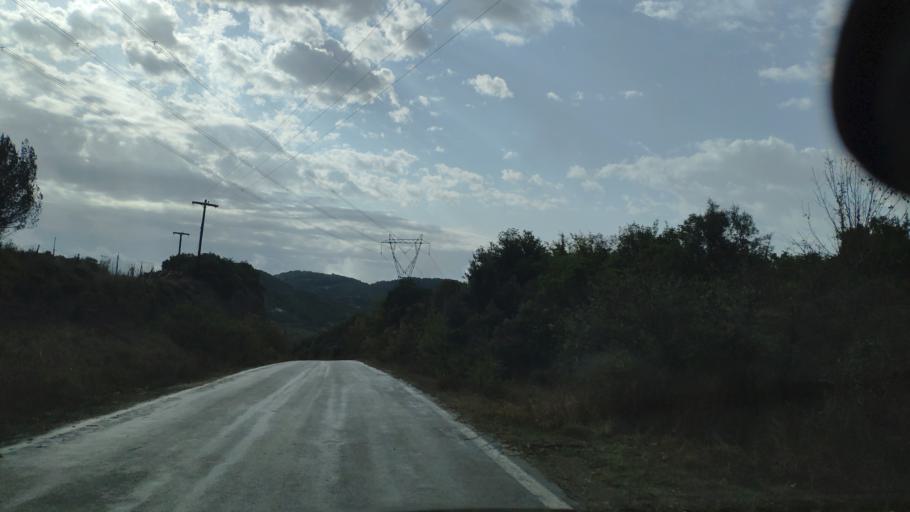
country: GR
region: West Greece
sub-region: Nomos Aitolias kai Akarnanias
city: Sardinia
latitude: 38.8755
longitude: 21.2726
